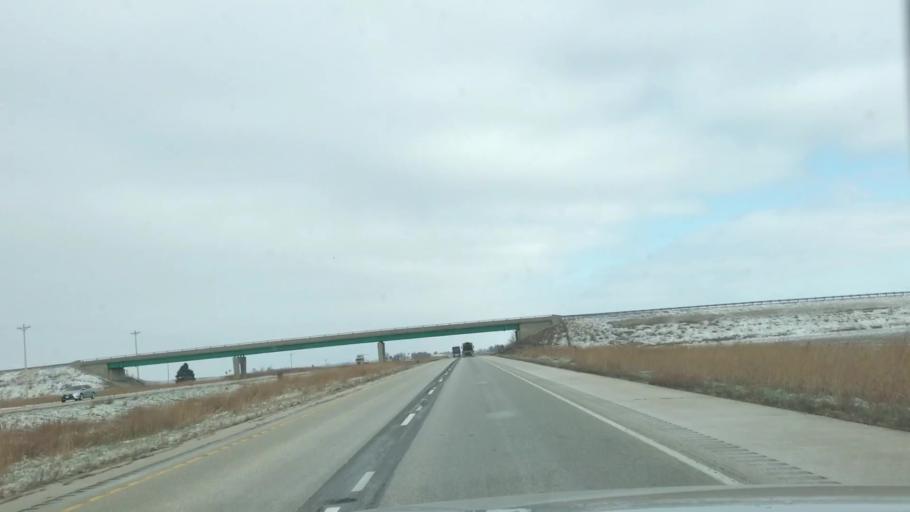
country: US
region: Illinois
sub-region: Sangamon County
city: Divernon
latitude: 39.4995
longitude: -89.6450
